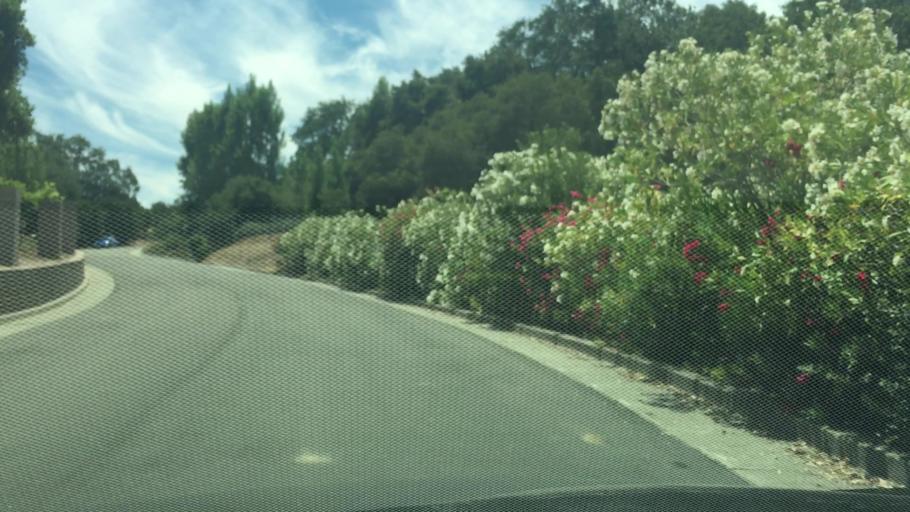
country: US
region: California
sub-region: San Mateo County
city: Ladera
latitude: 37.3703
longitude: -122.1757
